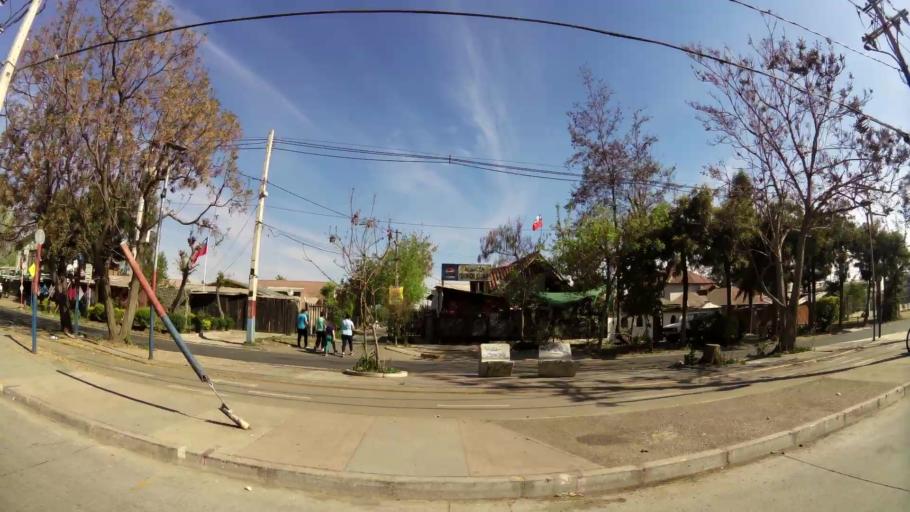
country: CL
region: Santiago Metropolitan
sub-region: Provincia de Santiago
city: Villa Presidente Frei, Nunoa, Santiago, Chile
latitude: -33.4755
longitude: -70.5765
